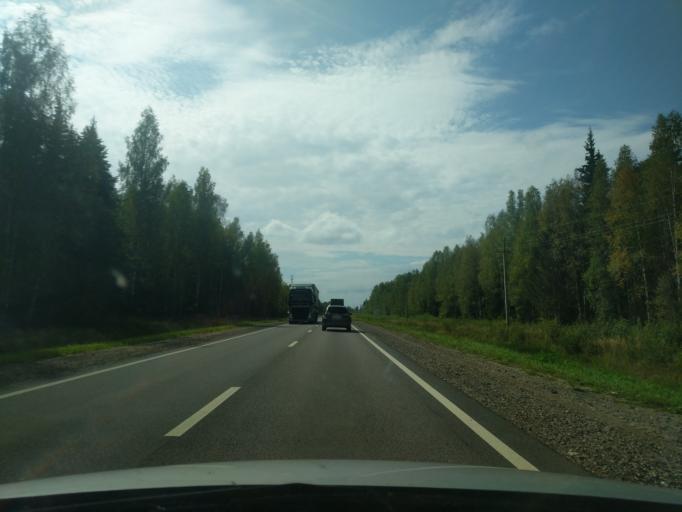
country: RU
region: Kostroma
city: Kadyy
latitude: 57.8039
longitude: 43.2124
